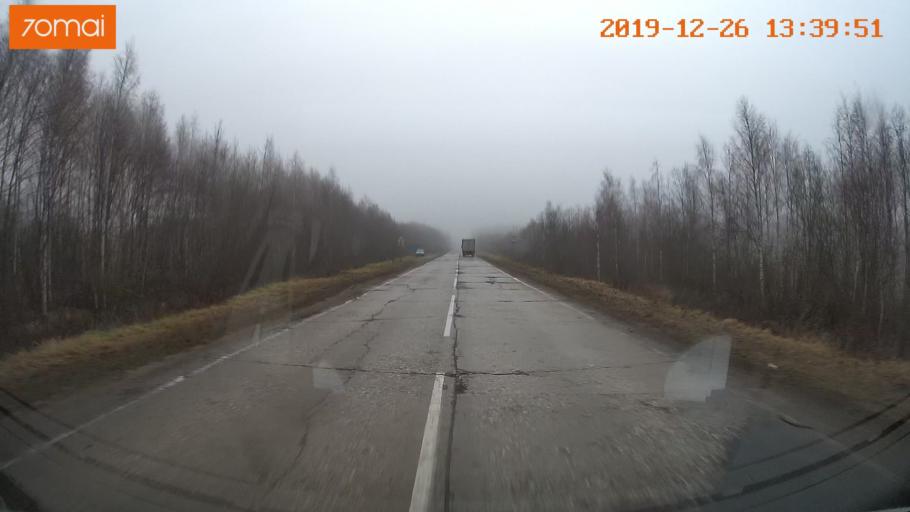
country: RU
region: Vologda
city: Sheksna
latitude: 58.7482
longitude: 38.4187
